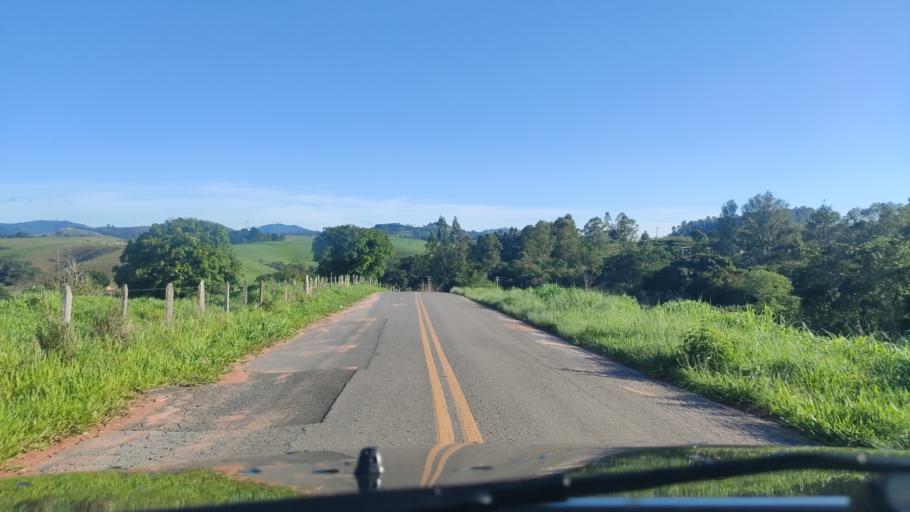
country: BR
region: Sao Paulo
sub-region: Aguas De Lindoia
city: Aguas de Lindoia
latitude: -22.5514
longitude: -46.6136
